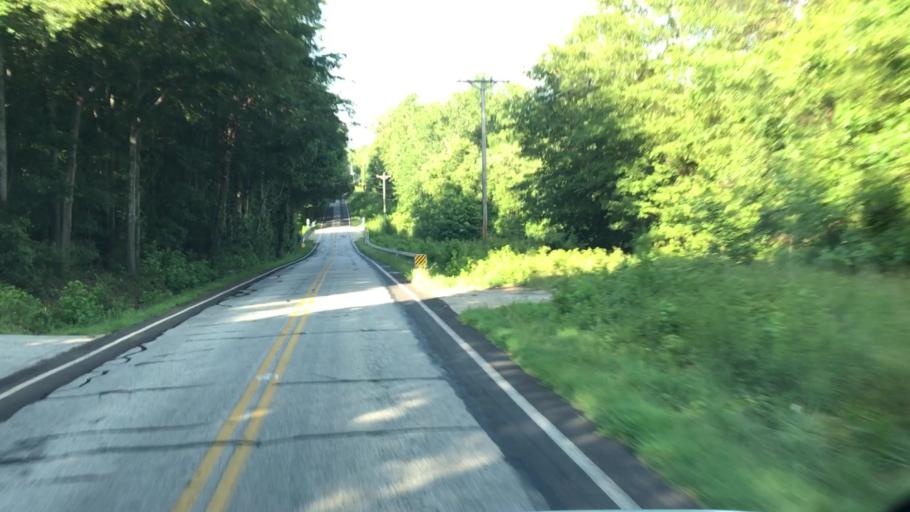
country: US
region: South Carolina
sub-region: Anderson County
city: Williamston
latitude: 34.6406
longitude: -82.4251
